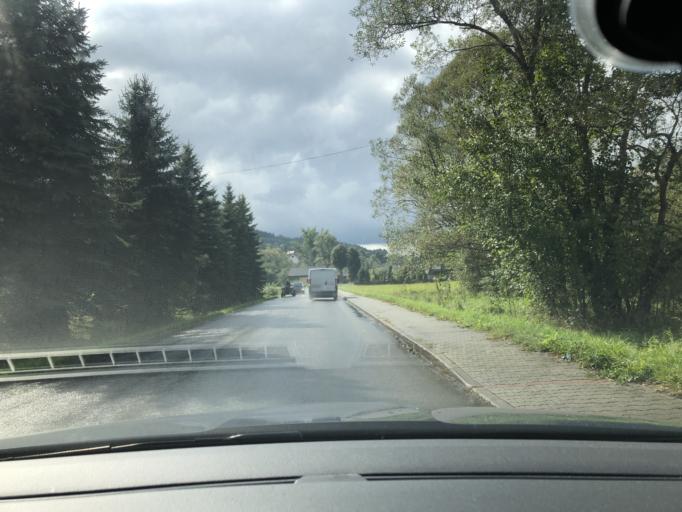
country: PL
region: Lesser Poland Voivodeship
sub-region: Powiat suski
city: Kukow
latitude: 49.7212
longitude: 19.4989
